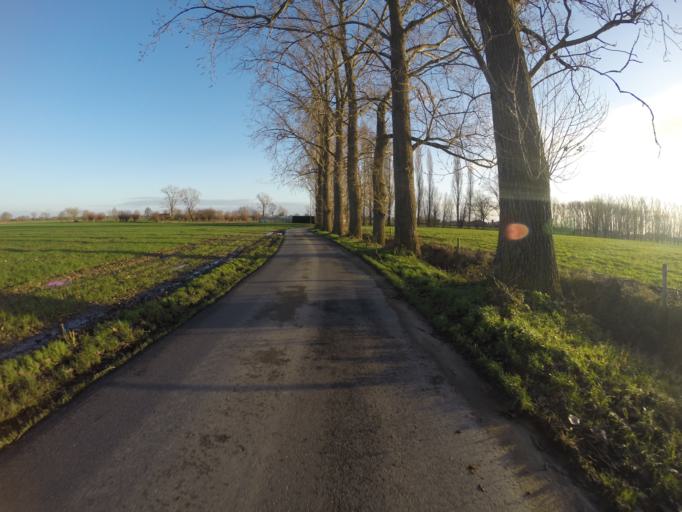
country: BE
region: Flanders
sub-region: Provincie Oost-Vlaanderen
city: Nevele
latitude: 51.0484
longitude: 3.4924
